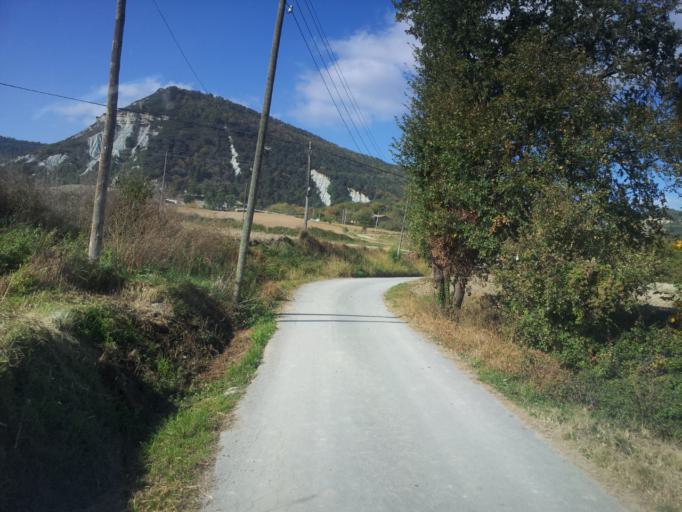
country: ES
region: Catalonia
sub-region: Provincia de Barcelona
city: Gurb
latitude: 41.9396
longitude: 2.2160
